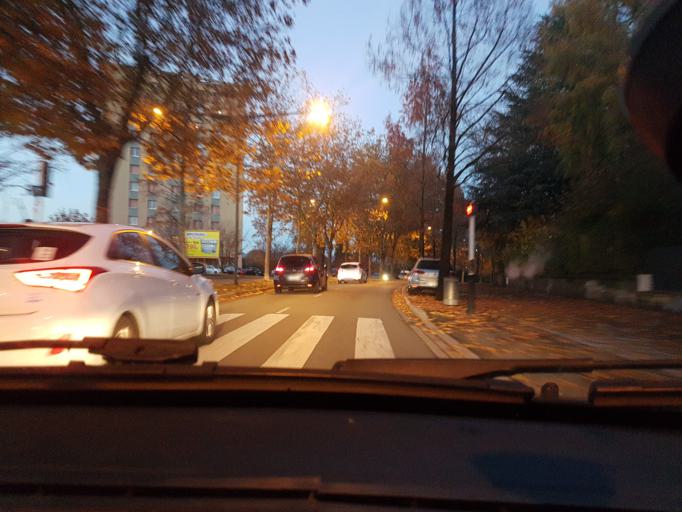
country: FR
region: Franche-Comte
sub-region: Territoire de Belfort
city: Bavilliers
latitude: 47.6386
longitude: 6.8387
